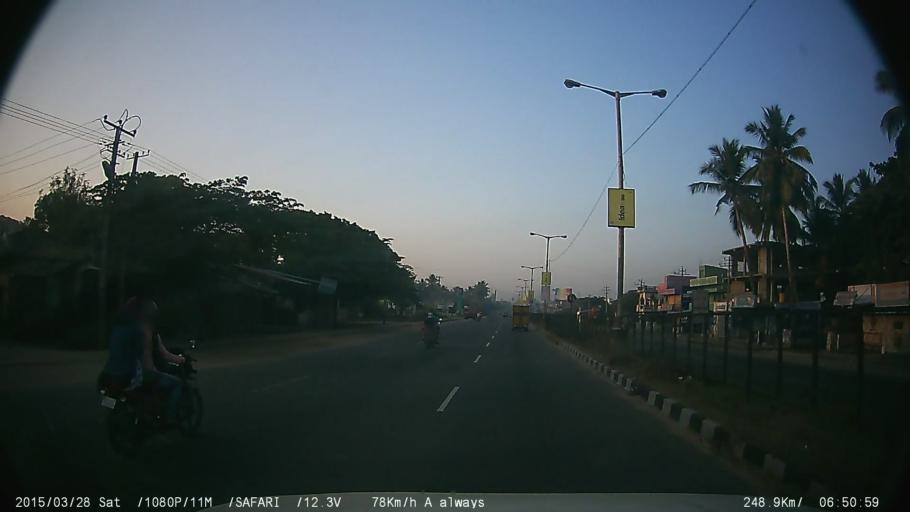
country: IN
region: Karnataka
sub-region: Mandya
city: Maddur
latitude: 12.6008
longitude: 77.0529
